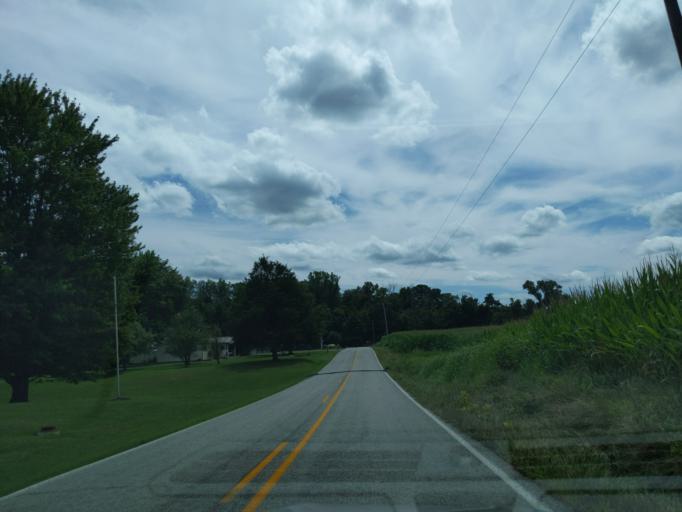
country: US
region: Indiana
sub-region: Ripley County
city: Osgood
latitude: 39.2180
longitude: -85.2680
